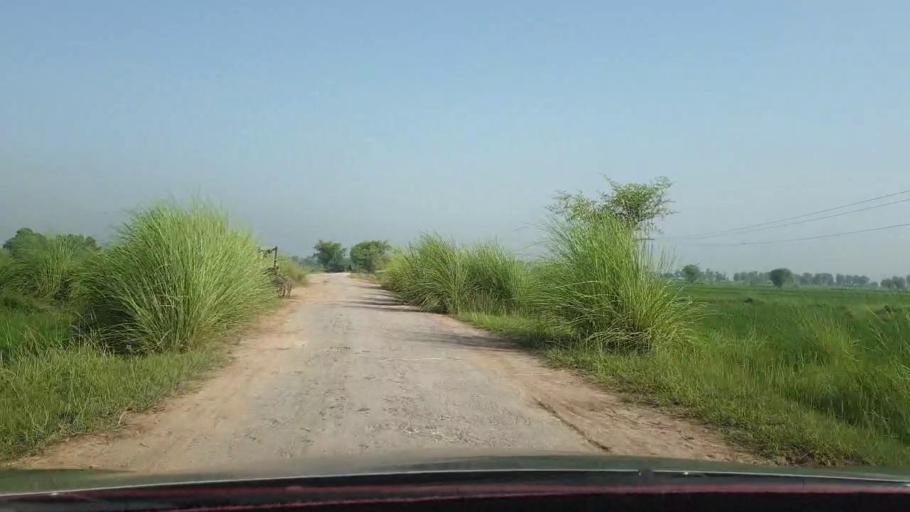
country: PK
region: Sindh
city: Nasirabad
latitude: 27.4429
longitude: 67.9201
